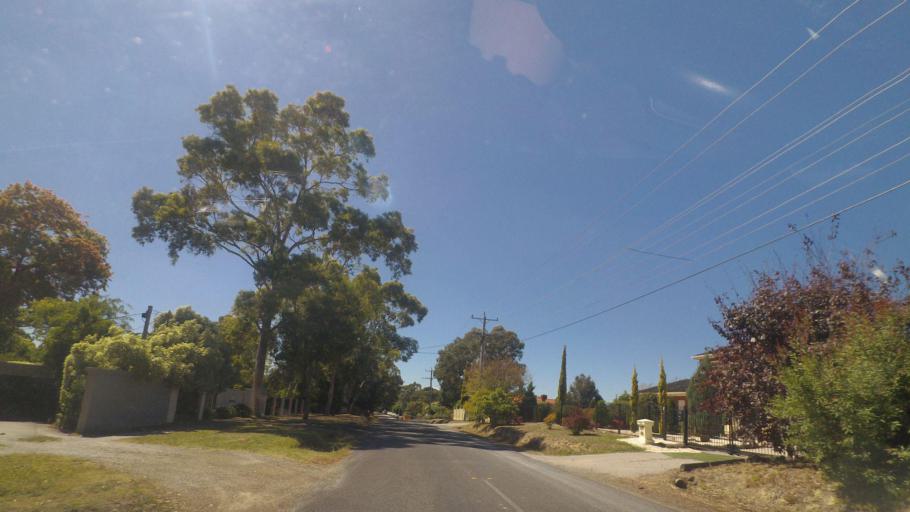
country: AU
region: Victoria
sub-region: Manningham
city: Donvale
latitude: -37.7959
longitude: 145.1818
